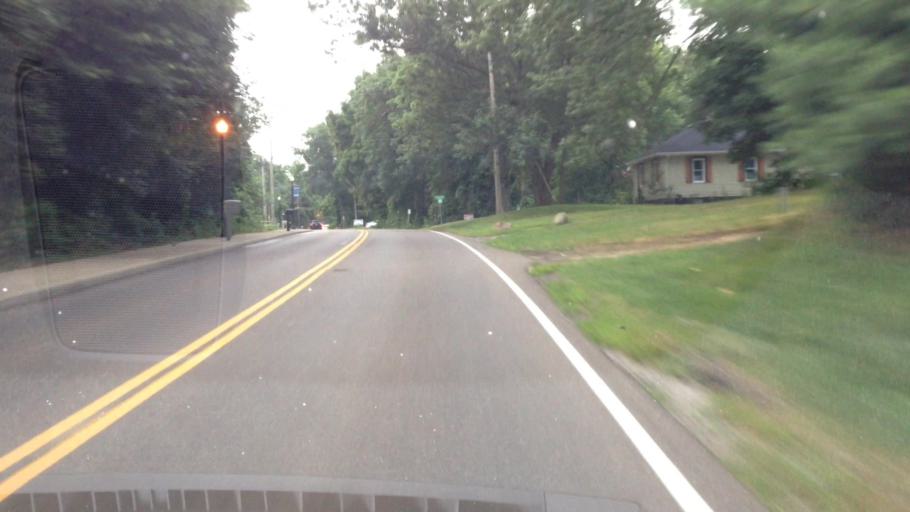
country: US
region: Ohio
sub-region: Summit County
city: Portage Lakes
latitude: 41.0001
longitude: -81.5408
